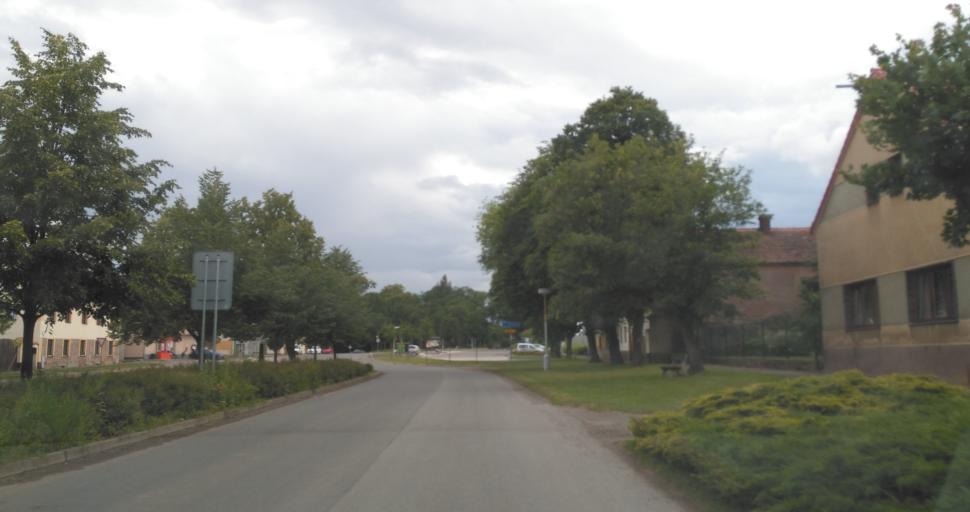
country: CZ
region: Central Bohemia
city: Hostomice
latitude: 49.8535
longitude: 14.0375
